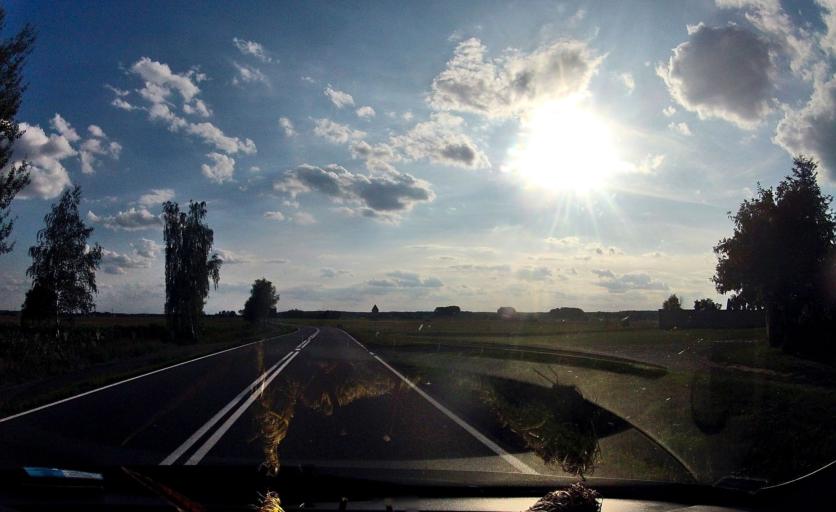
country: PL
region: Opole Voivodeship
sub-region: Powiat oleski
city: Praszka
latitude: 51.0528
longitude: 18.4301
